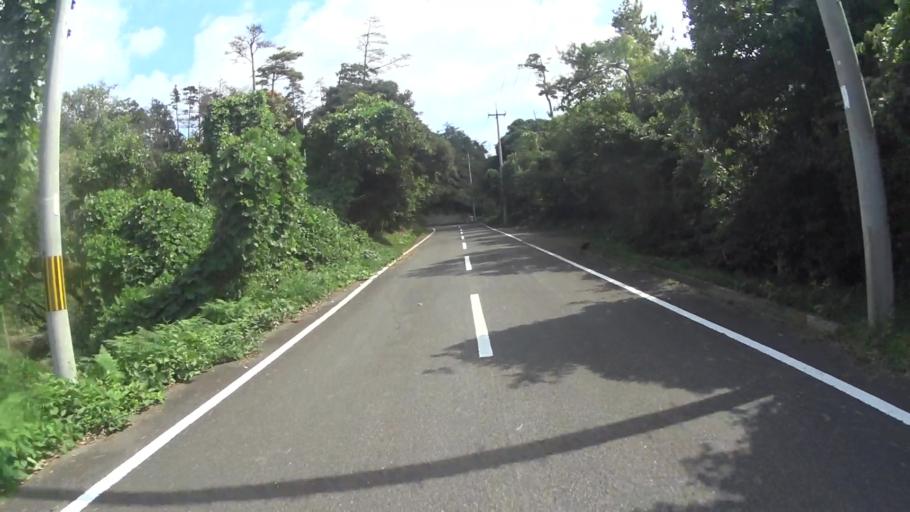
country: JP
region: Kyoto
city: Miyazu
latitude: 35.7467
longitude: 135.1711
